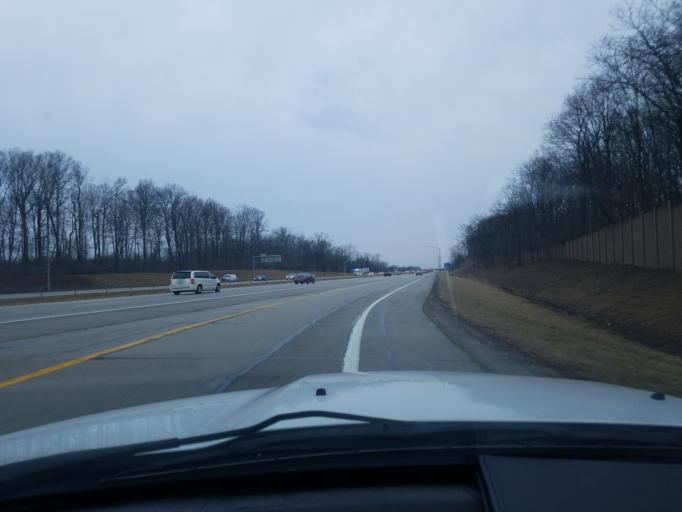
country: US
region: Ohio
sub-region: Greene County
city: Bellbrook
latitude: 39.6559
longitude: -84.1135
